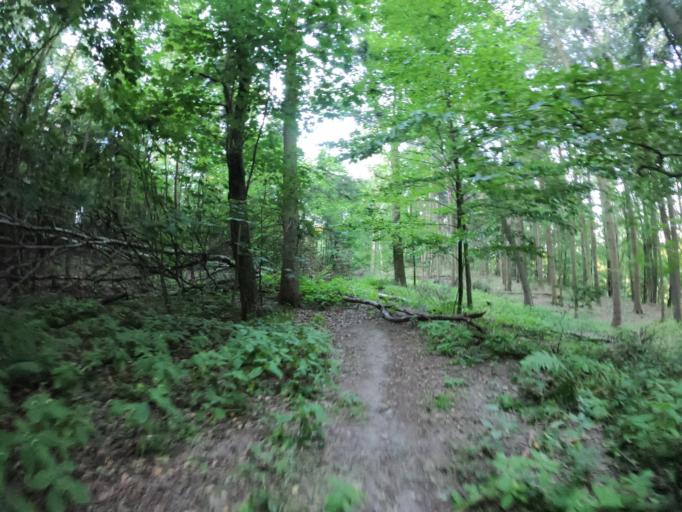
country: PL
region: West Pomeranian Voivodeship
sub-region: Powiat drawski
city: Zlocieniec
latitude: 53.6505
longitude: 15.9211
